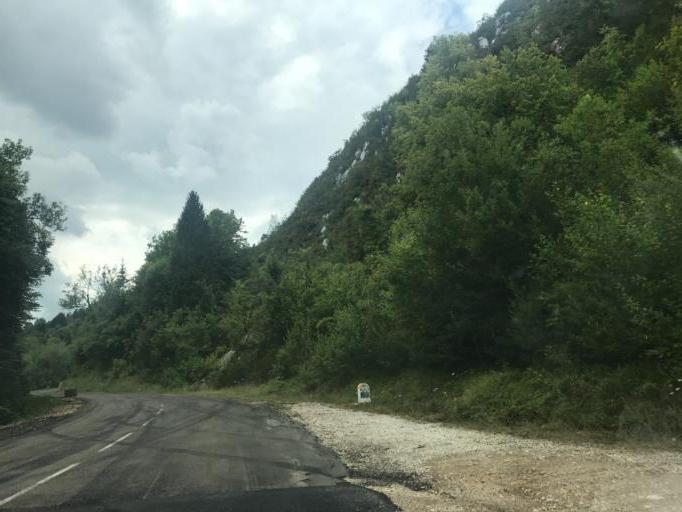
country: FR
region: Franche-Comte
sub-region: Departement du Jura
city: Saint-Claude
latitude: 46.3590
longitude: 5.8484
